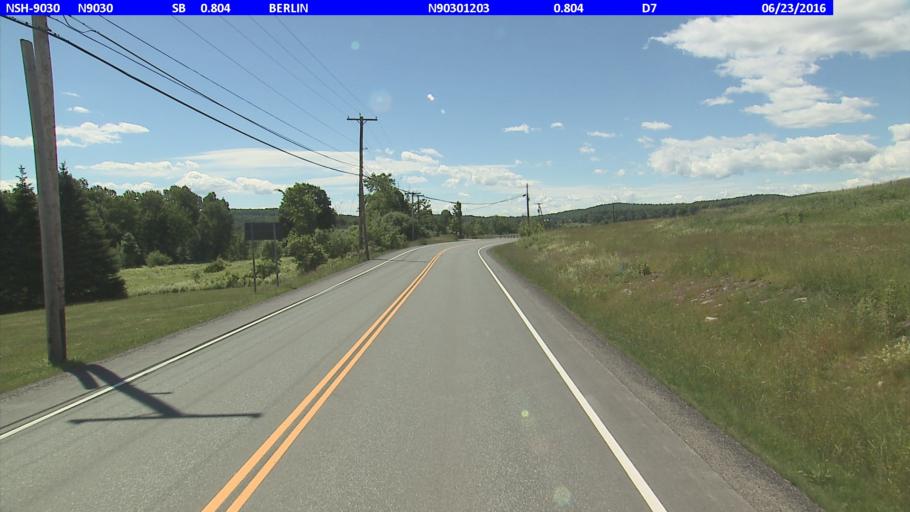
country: US
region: Vermont
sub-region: Washington County
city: Montpelier
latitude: 44.2134
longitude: -72.5556
